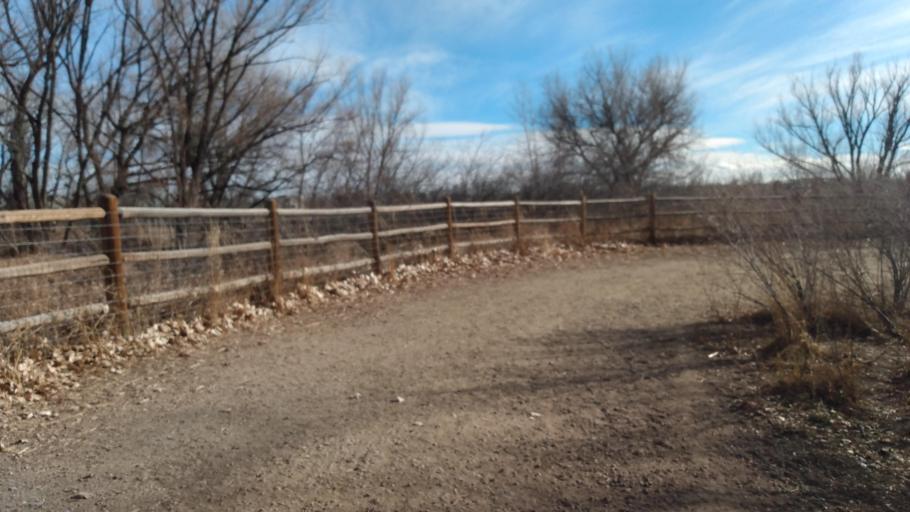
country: US
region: Colorado
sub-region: Boulder County
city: Gunbarrel
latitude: 40.0610
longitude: -105.1991
